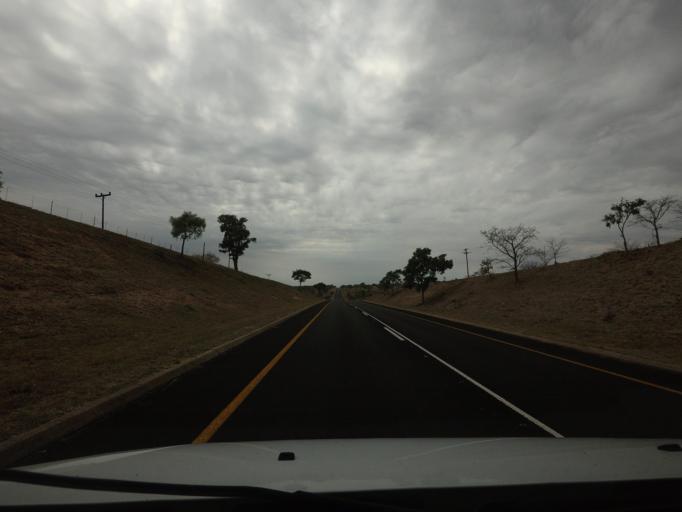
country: ZA
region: Limpopo
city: Thulamahashi
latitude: -24.5634
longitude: 31.1373
